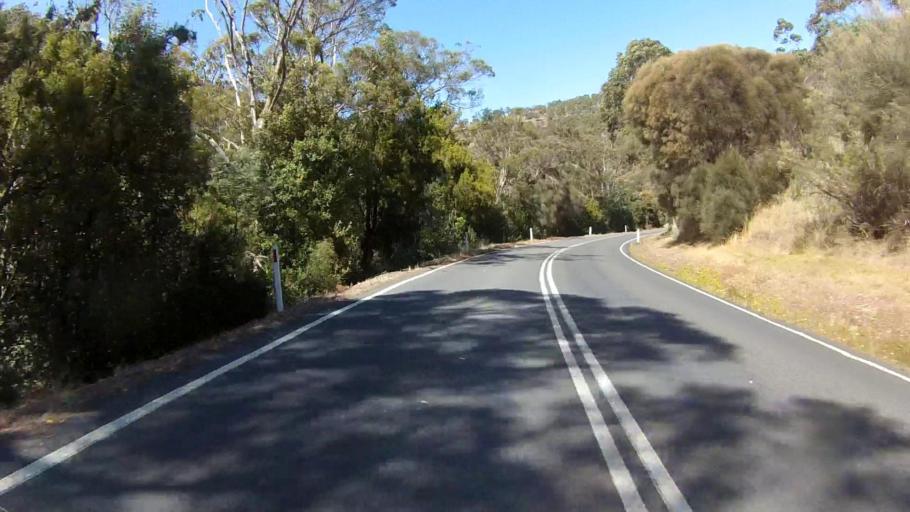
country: AU
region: Tasmania
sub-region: Derwent Valley
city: New Norfolk
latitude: -42.6796
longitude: 146.7664
